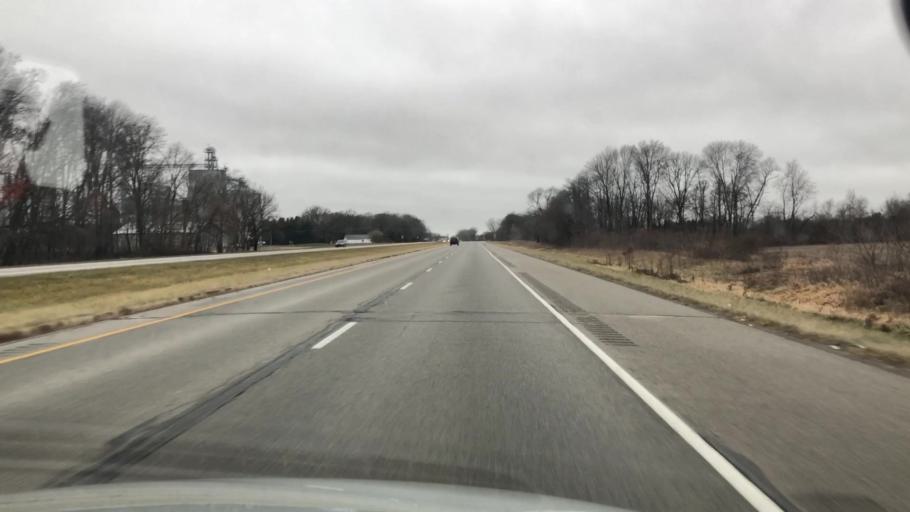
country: US
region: Indiana
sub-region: Kosciusko County
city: Mentone
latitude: 41.2699
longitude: -86.0063
